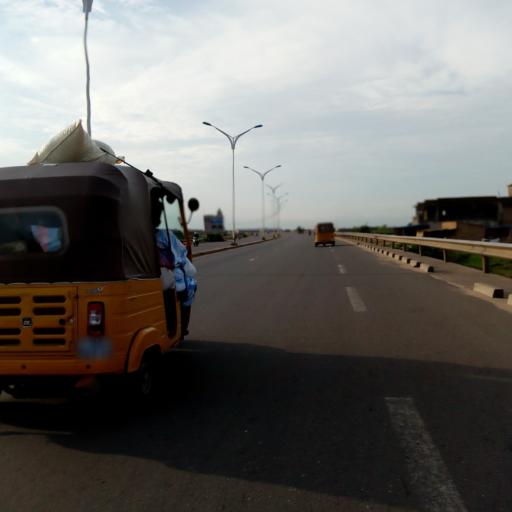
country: TG
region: Maritime
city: Lome
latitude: 6.1833
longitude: 1.2798
